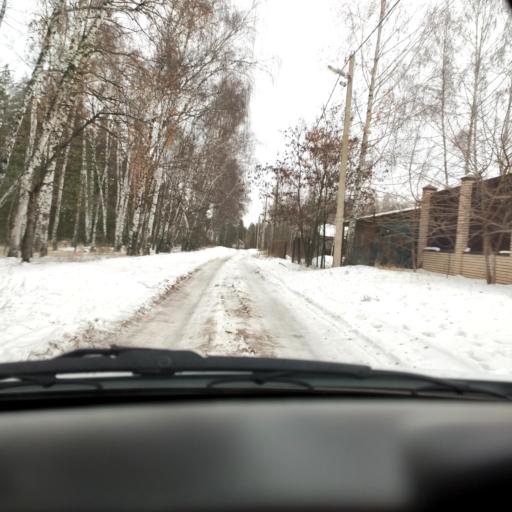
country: RU
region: Voronezj
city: Ramon'
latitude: 51.8799
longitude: 39.2654
